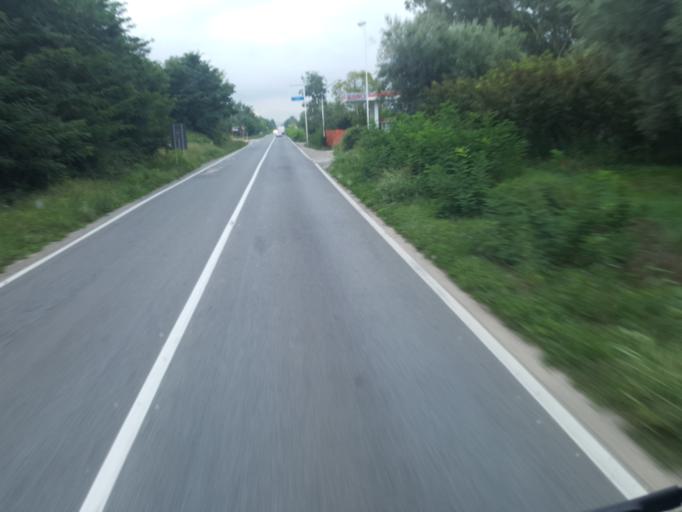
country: IT
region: Campania
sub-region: Provincia di Caserta
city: Pignataro Maggiore
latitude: 41.1707
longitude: 14.1422
